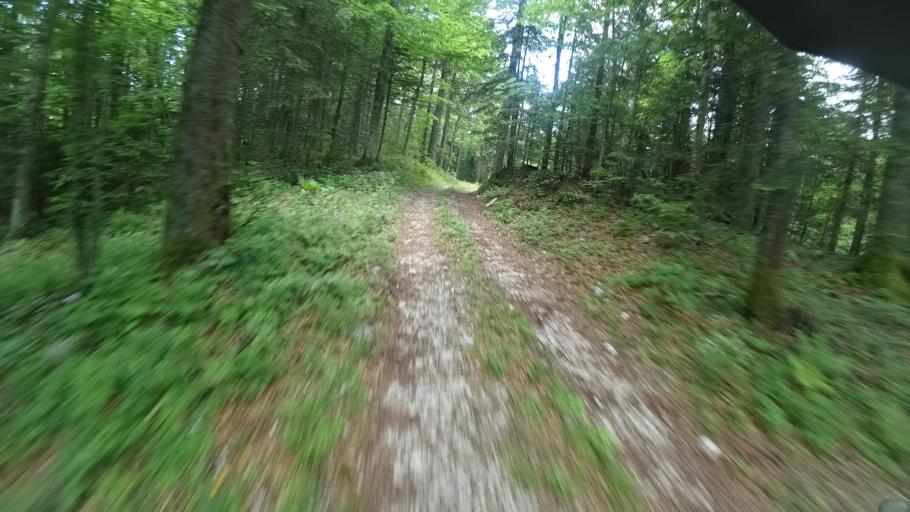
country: HR
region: Zadarska
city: Gracac
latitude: 44.4796
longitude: 15.8900
